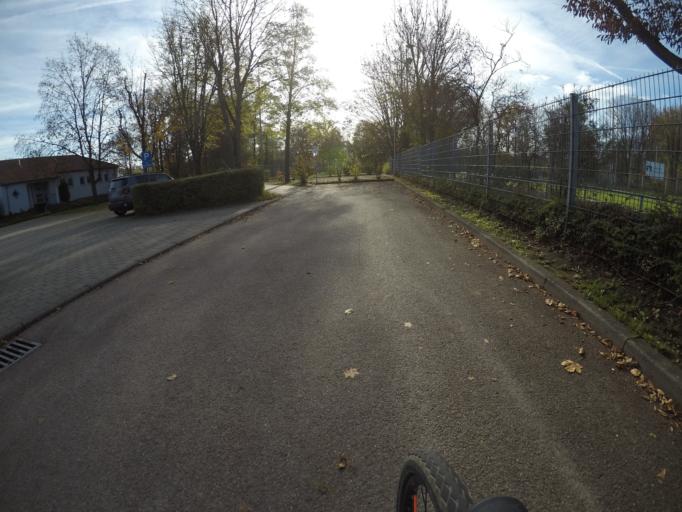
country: DE
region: Baden-Wuerttemberg
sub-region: Regierungsbezirk Stuttgart
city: Weinstadt-Endersbach
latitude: 48.8181
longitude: 9.3504
